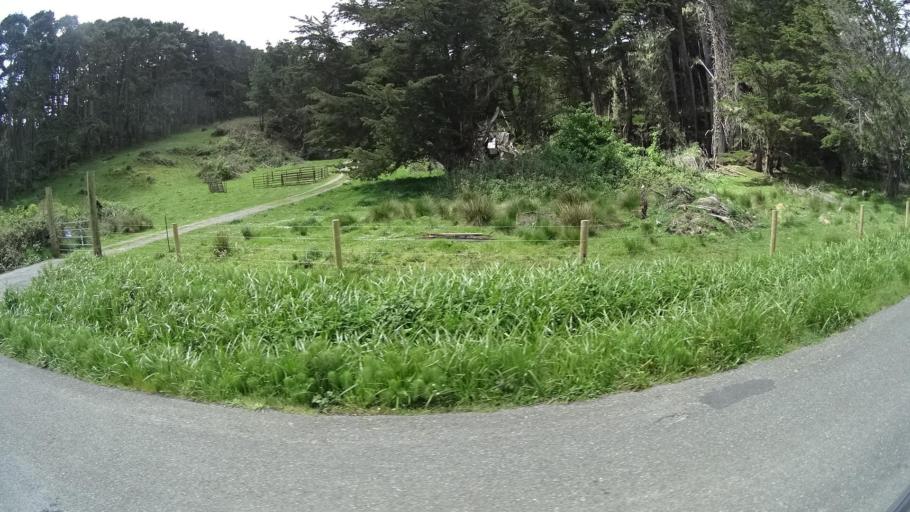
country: US
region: California
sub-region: Humboldt County
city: Humboldt Hill
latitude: 40.6827
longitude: -124.2308
